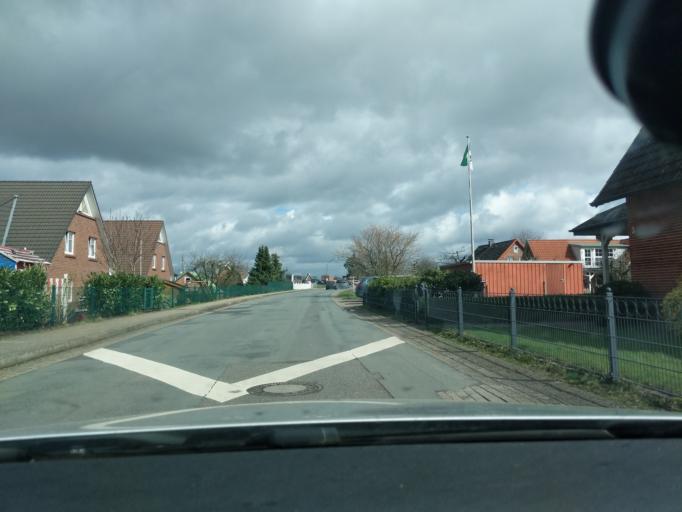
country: DE
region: Lower Saxony
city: Grunendeich
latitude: 53.5703
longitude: 9.6264
